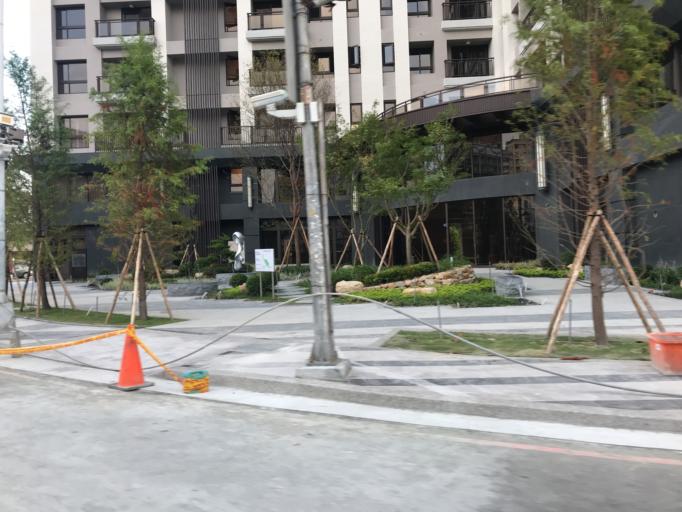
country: TW
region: Taiwan
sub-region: Taichung City
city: Taichung
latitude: 24.1152
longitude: 120.6923
